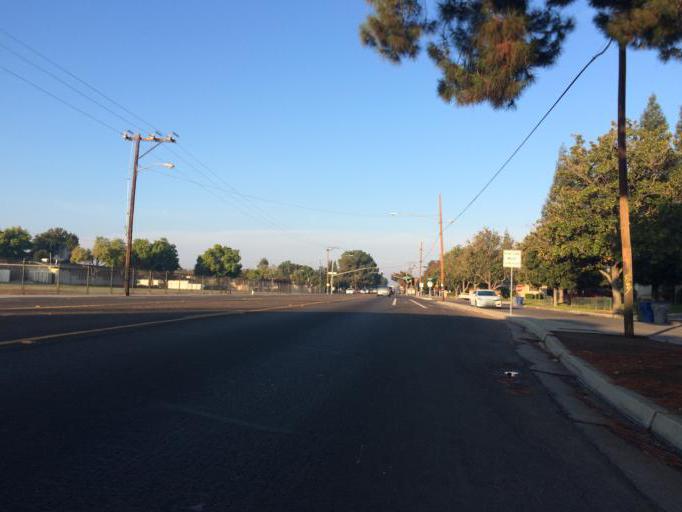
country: US
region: California
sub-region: Fresno County
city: Fresno
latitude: 36.8014
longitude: -119.7614
